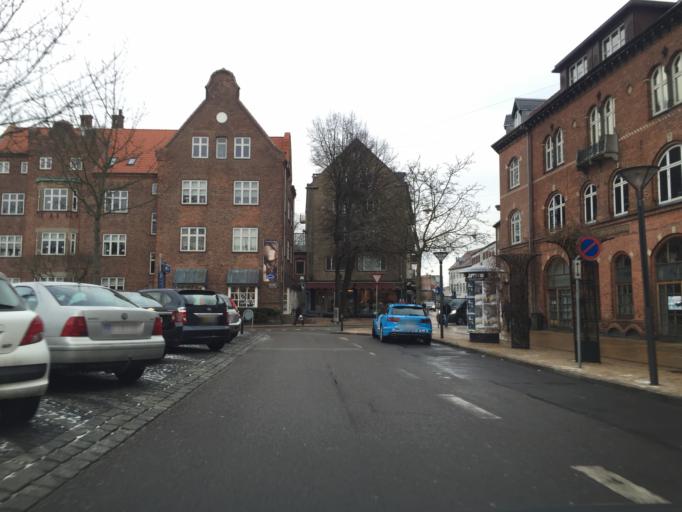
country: DK
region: South Denmark
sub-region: Odense Kommune
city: Odense
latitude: 55.3974
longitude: 10.3873
